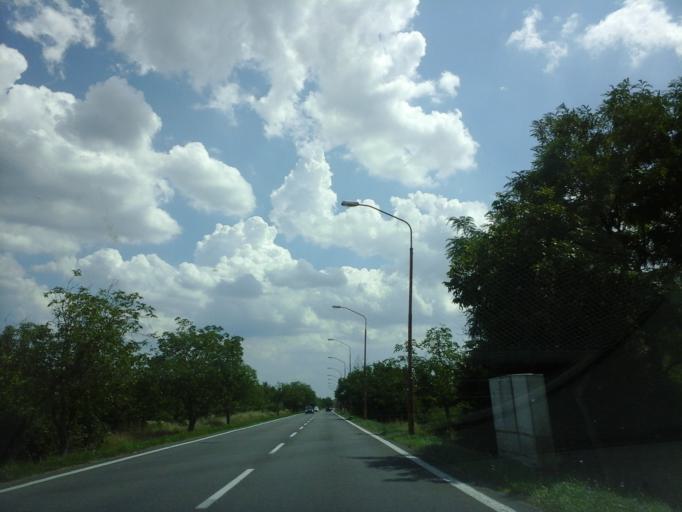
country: HU
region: Gyor-Moson-Sopron
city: Rajka
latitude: 48.0401
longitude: 17.1592
